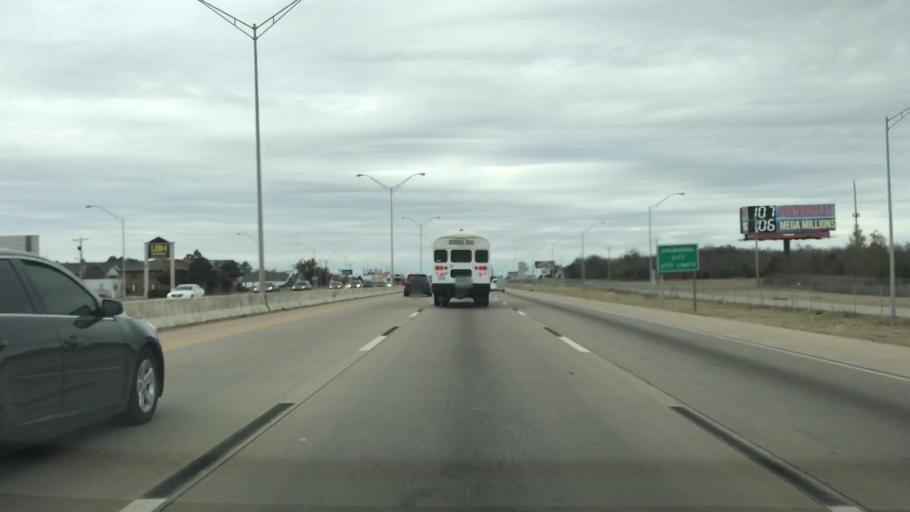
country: US
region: Oklahoma
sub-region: Cleveland County
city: Moore
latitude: 35.3695
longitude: -97.4948
